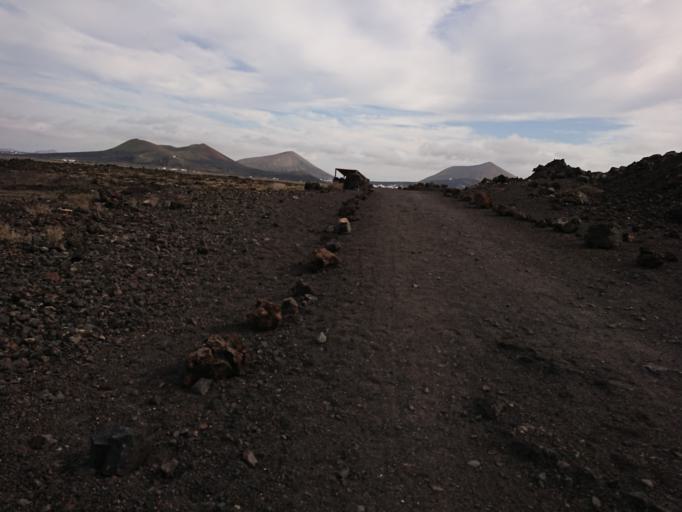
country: ES
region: Canary Islands
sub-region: Provincia de Las Palmas
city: Tinajo
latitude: 29.0089
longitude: -13.6767
